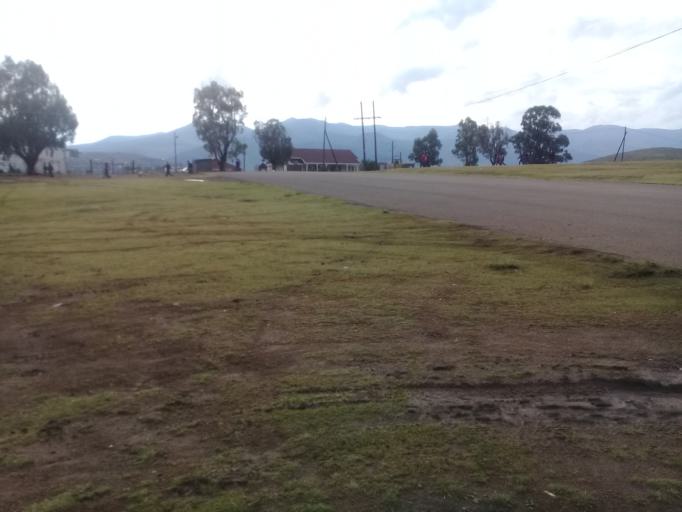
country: LS
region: Mokhotlong
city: Mokhotlong
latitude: -29.2805
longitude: 29.0664
